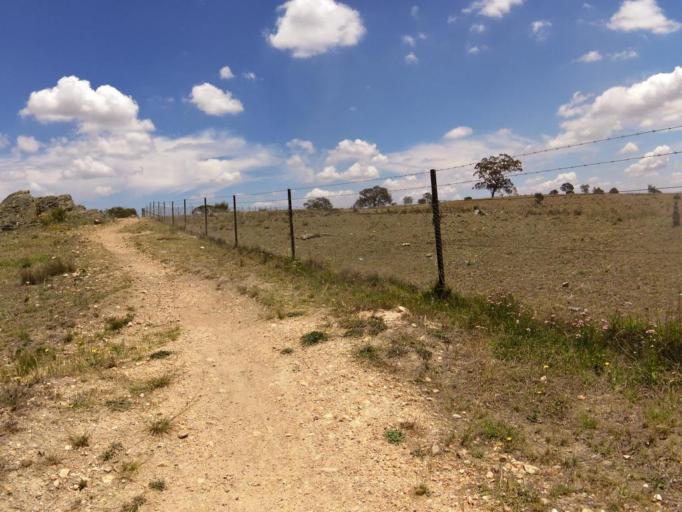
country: AU
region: Australian Capital Territory
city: Kaleen
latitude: -35.1448
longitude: 149.1484
